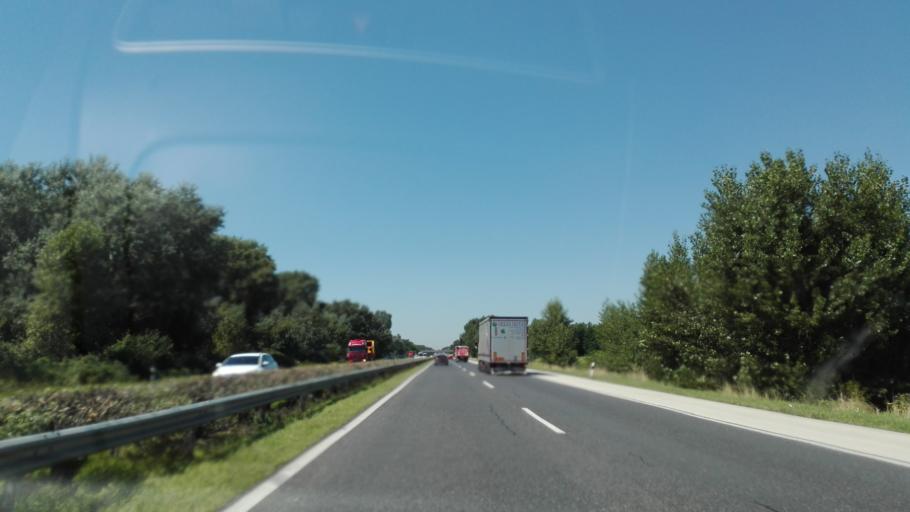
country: HU
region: Komarom-Esztergom
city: Vertesszolos
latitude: 47.6083
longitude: 18.3657
